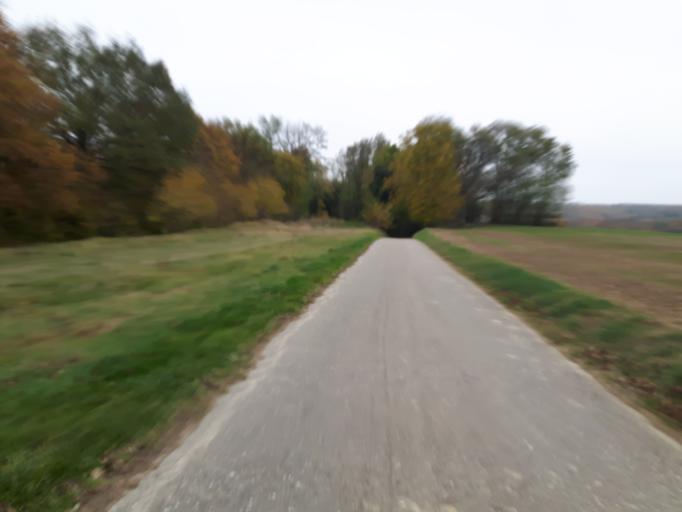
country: DE
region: Baden-Wuerttemberg
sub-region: Karlsruhe Region
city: Ostringen
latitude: 49.1888
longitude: 8.7329
